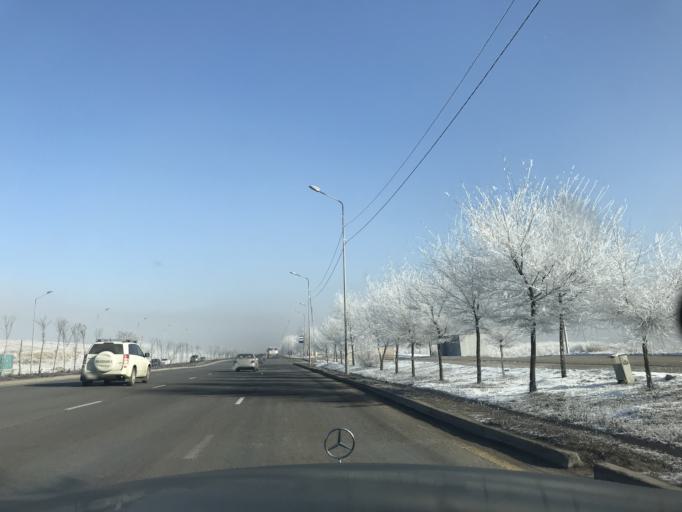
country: KZ
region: Almaty Oblysy
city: Burunday
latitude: 43.2893
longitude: 76.8277
